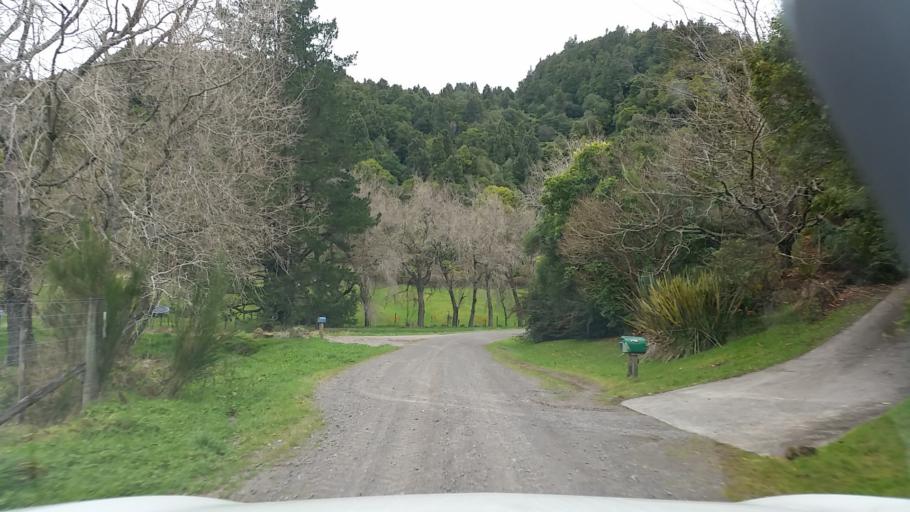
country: NZ
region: Bay of Plenty
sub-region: Rotorua District
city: Rotorua
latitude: -38.1589
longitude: 176.3693
